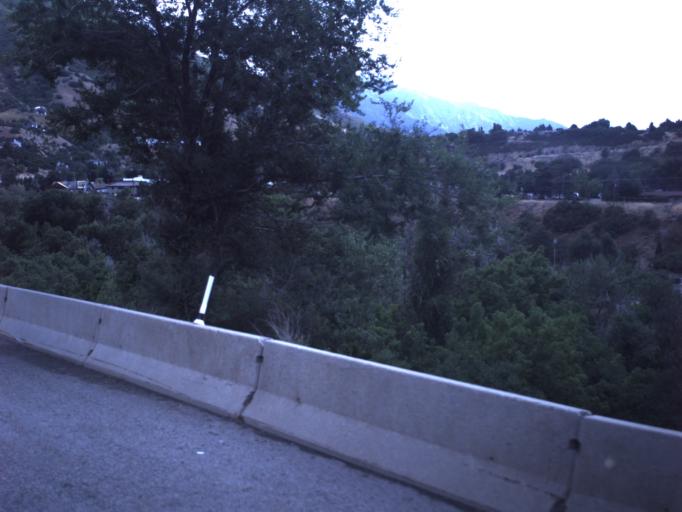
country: US
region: Utah
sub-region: Salt Lake County
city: Cottonwood Heights
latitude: 40.6233
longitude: -111.7943
